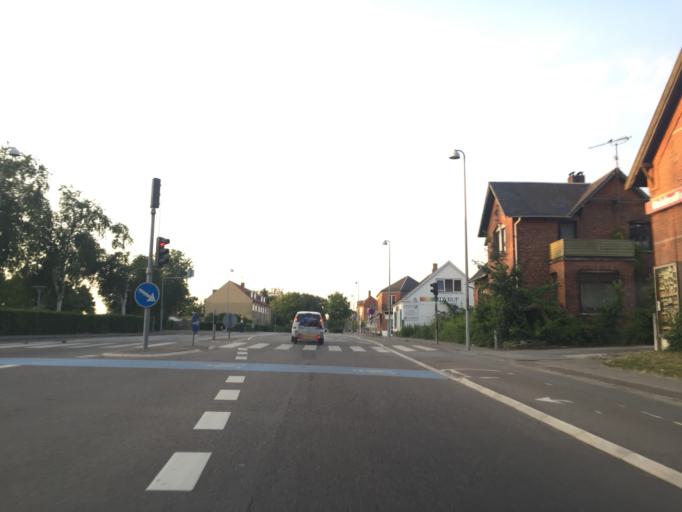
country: DK
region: Capital Region
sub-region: Hoje-Taastrup Kommune
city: Taastrup
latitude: 55.6531
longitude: 12.3045
